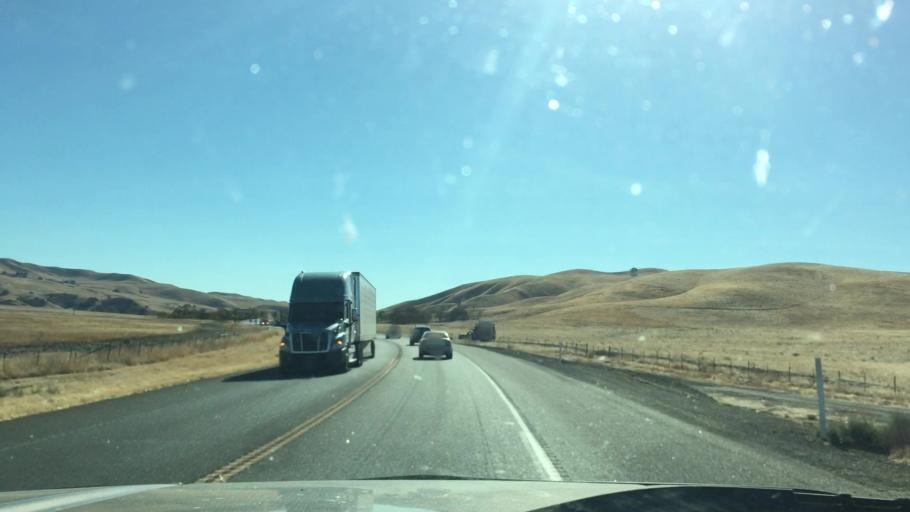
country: US
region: California
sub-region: San Luis Obispo County
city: Shandon
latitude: 35.7315
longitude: -120.2922
